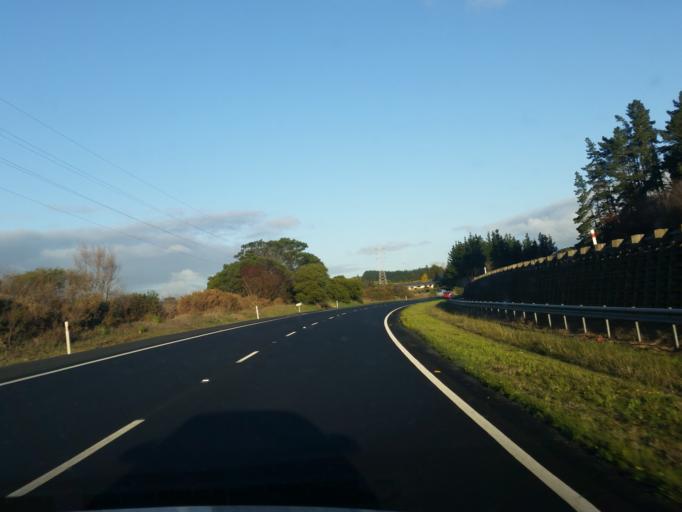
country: NZ
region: Auckland
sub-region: Auckland
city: Pukekohe East
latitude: -37.2541
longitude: 175.0369
